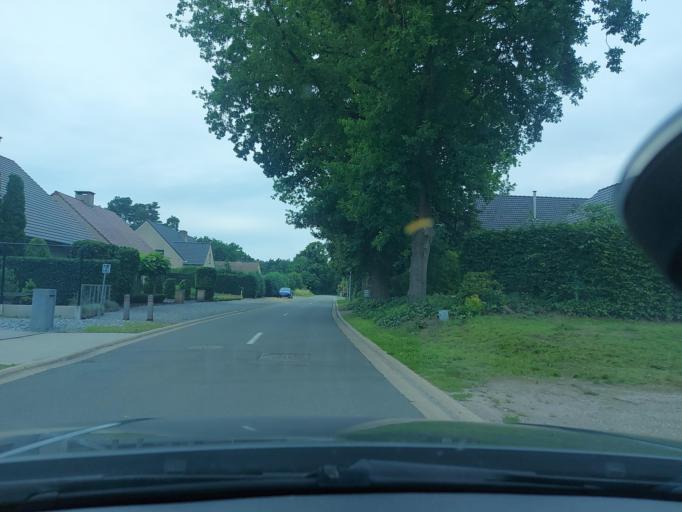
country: BE
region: Flanders
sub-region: Provincie Antwerpen
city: Balen
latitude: 51.1729
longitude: 5.2137
